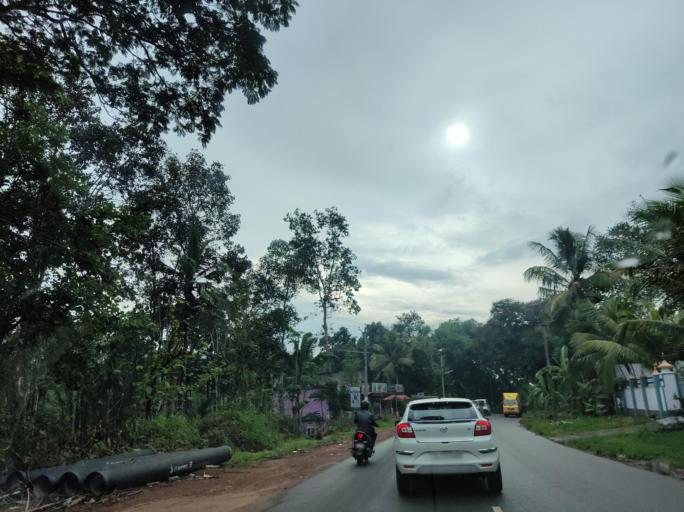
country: IN
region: Kerala
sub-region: Pattanamtitta
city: Adur
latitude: 9.1634
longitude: 76.7005
